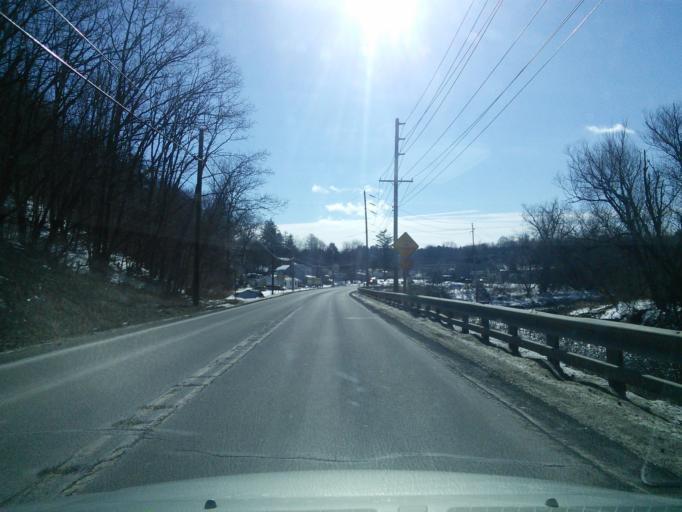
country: US
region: Pennsylvania
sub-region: Centre County
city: Milesburg
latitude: 40.9281
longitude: -77.7808
